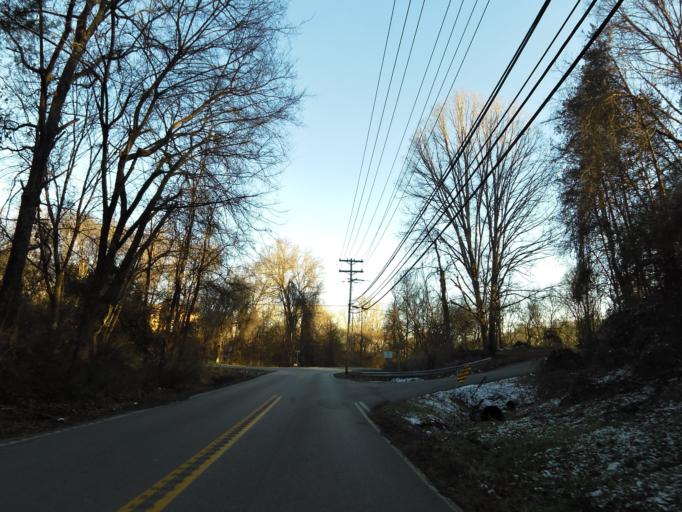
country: US
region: Tennessee
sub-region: Knox County
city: Farragut
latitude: 35.8777
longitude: -84.1216
